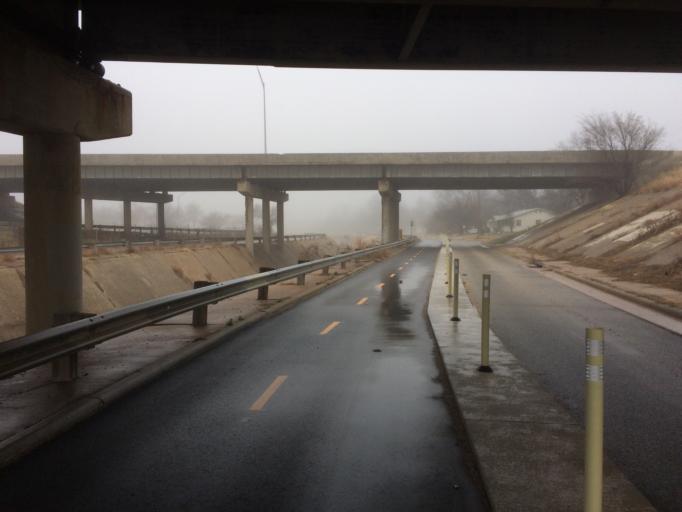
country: US
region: Oklahoma
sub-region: Oklahoma County
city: Oklahoma City
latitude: 35.4782
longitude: -97.5760
